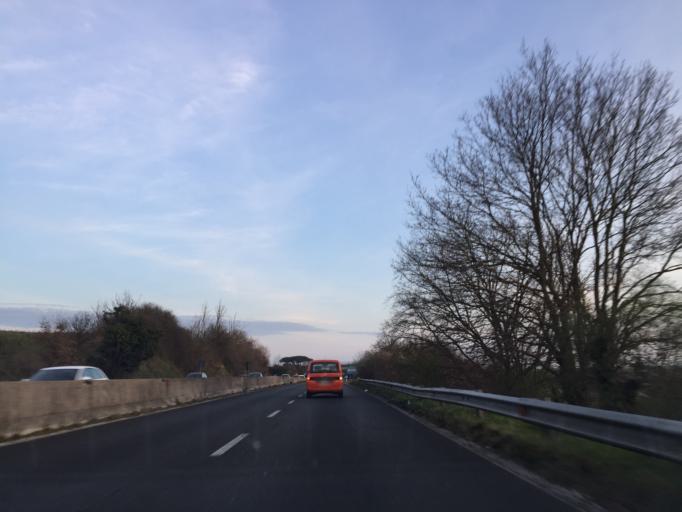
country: IT
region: Latium
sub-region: Citta metropolitana di Roma Capitale
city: Formello
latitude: 42.0344
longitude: 12.4272
